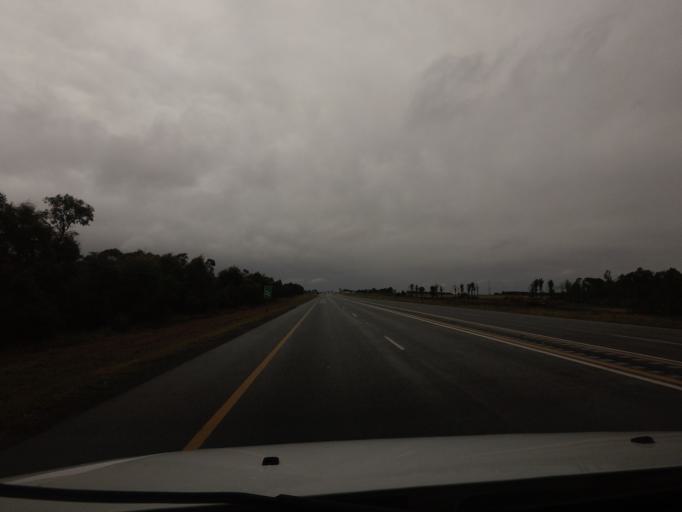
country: ZA
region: Mpumalanga
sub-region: Nkangala District Municipality
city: Belfast
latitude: -25.7190
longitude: 30.0488
